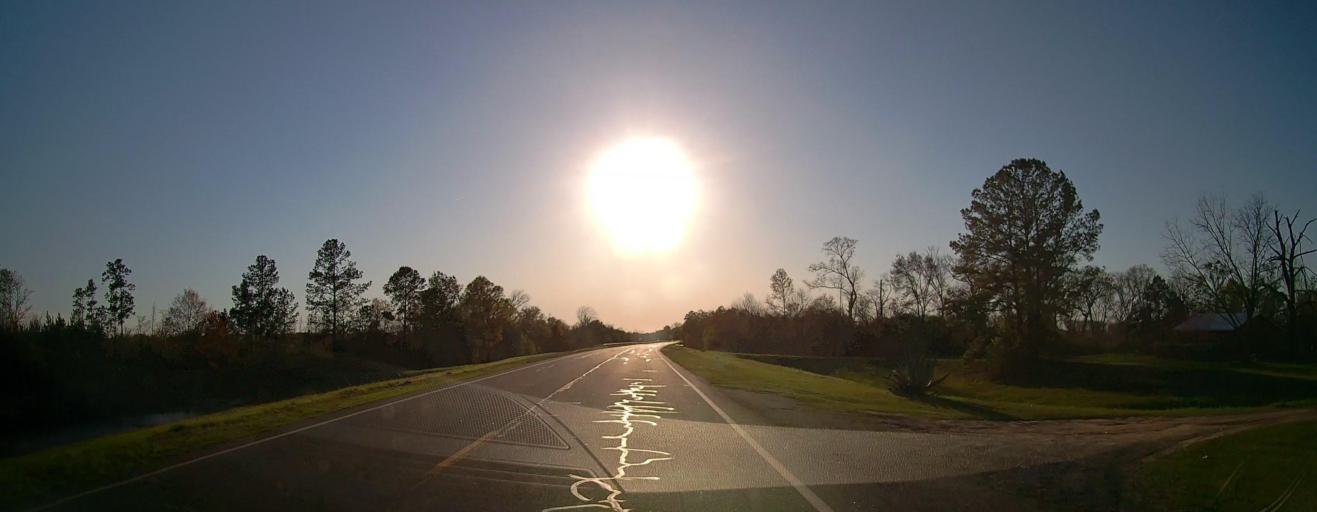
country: US
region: Georgia
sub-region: Wilcox County
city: Abbeville
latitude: 31.9989
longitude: -83.2654
